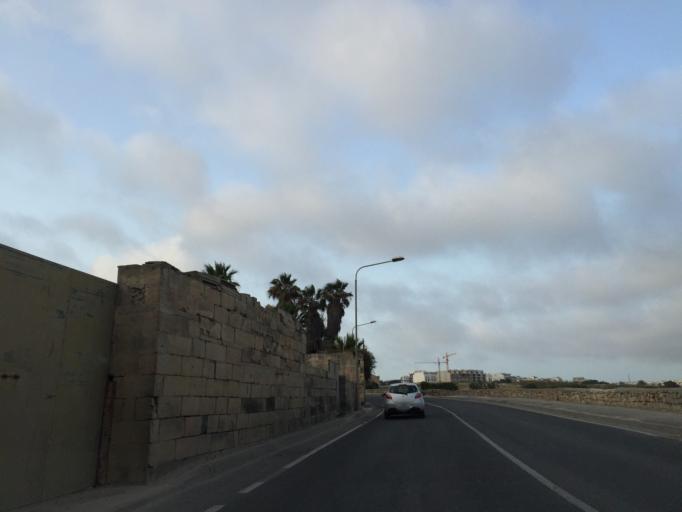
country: MT
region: L-Imtarfa
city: Imtarfa
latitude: 35.9063
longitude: 14.4089
